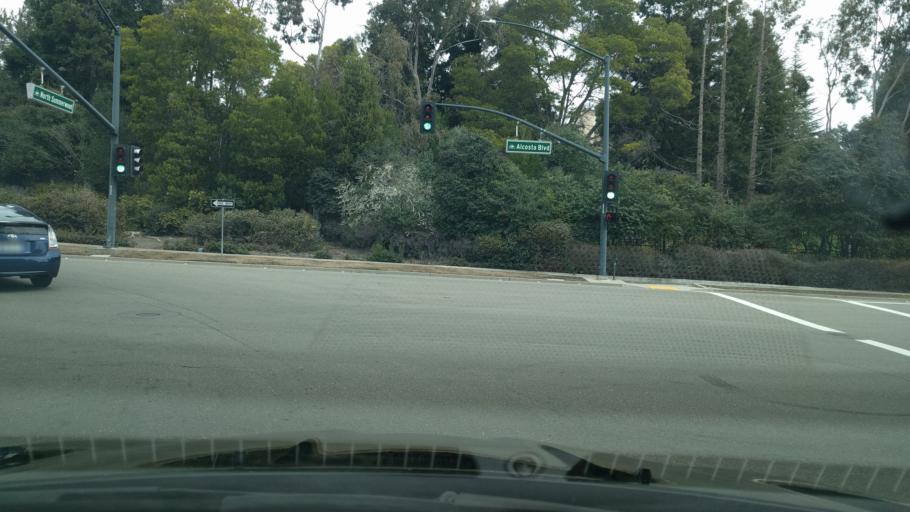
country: US
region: California
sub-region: Contra Costa County
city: San Ramon
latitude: 37.7609
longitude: -121.9455
